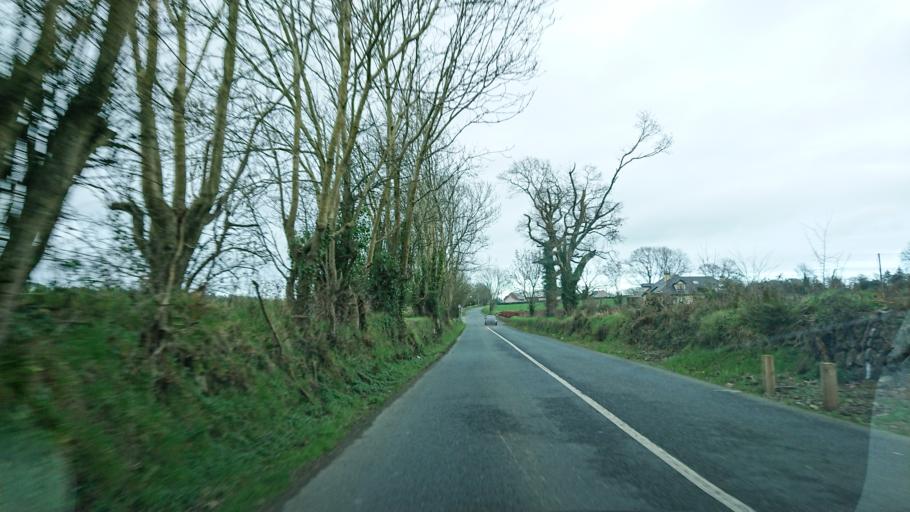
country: IE
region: Leinster
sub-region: Kilkenny
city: Mooncoin
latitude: 52.2254
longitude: -7.2381
